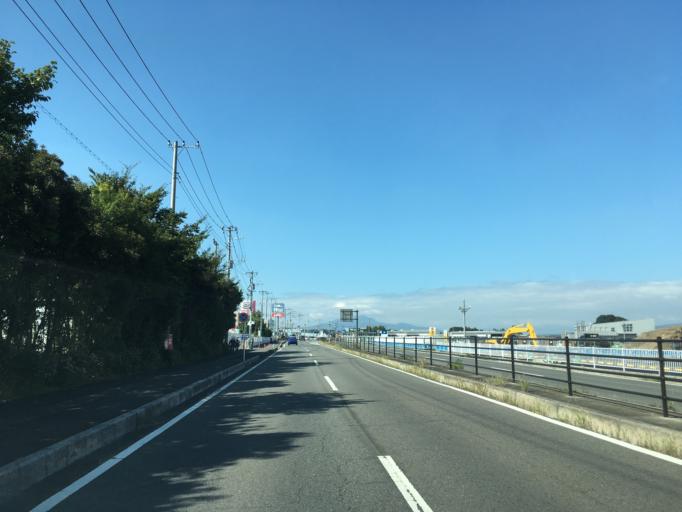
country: JP
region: Gunma
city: Kanekomachi
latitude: 36.3903
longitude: 139.0082
